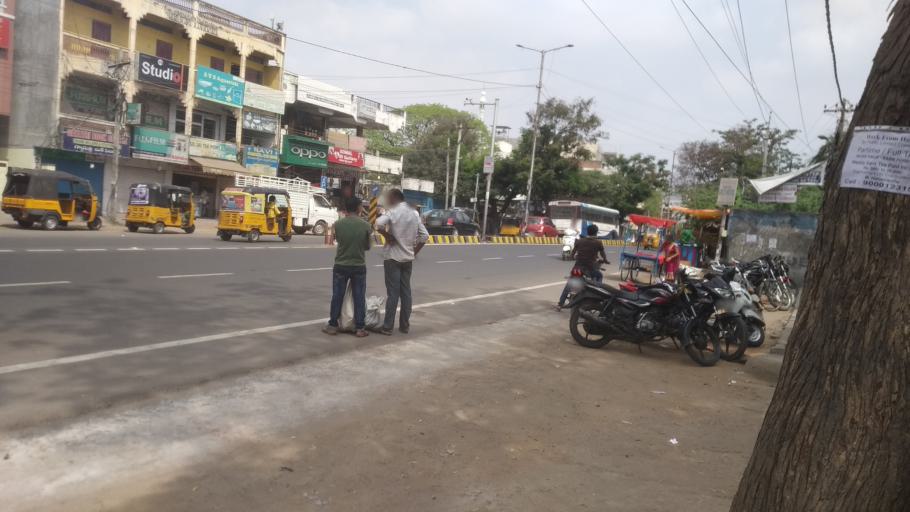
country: IN
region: Telangana
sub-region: Rangareddi
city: Gaddi Annaram
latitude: 17.3464
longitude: 78.5083
